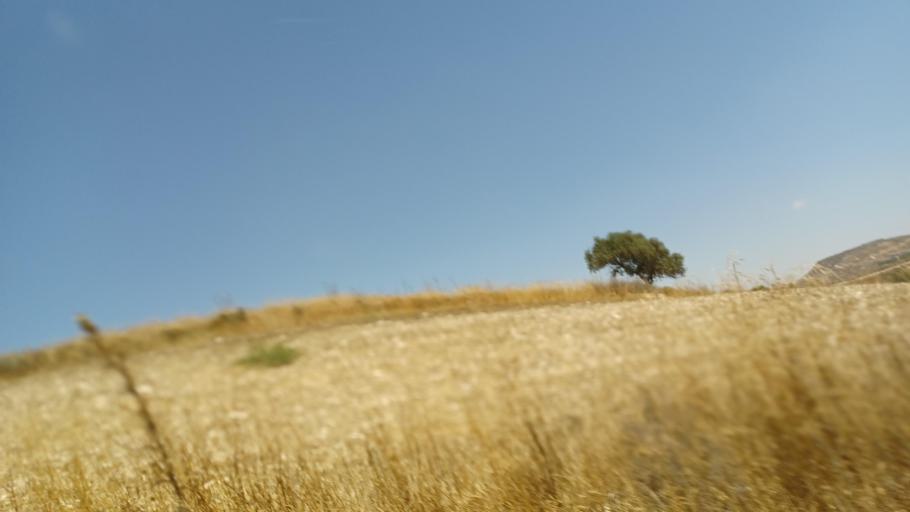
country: CY
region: Lefkosia
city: Lympia
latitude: 34.9917
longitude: 33.4847
